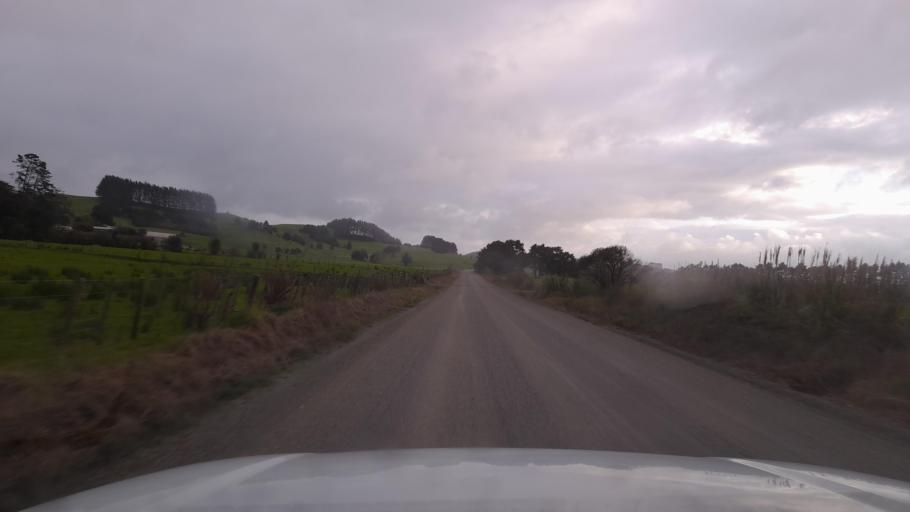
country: NZ
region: Northland
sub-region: Whangarei
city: Maungatapere
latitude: -35.6284
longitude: 174.1969
